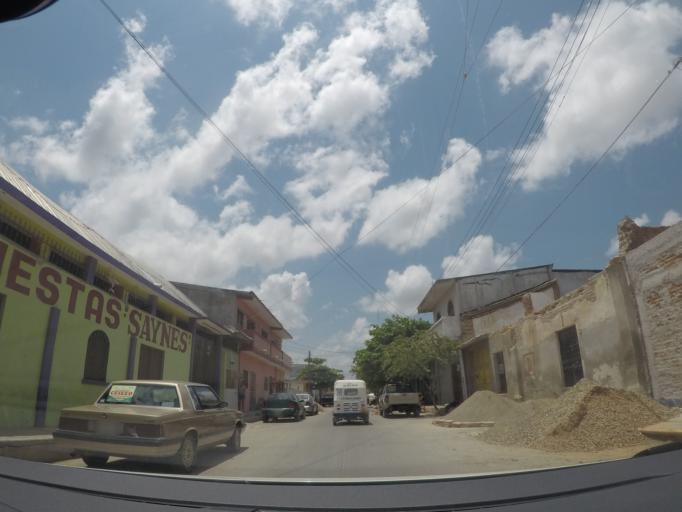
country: MX
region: Oaxaca
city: Juchitan de Zaragoza
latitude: 16.4391
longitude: -95.0232
